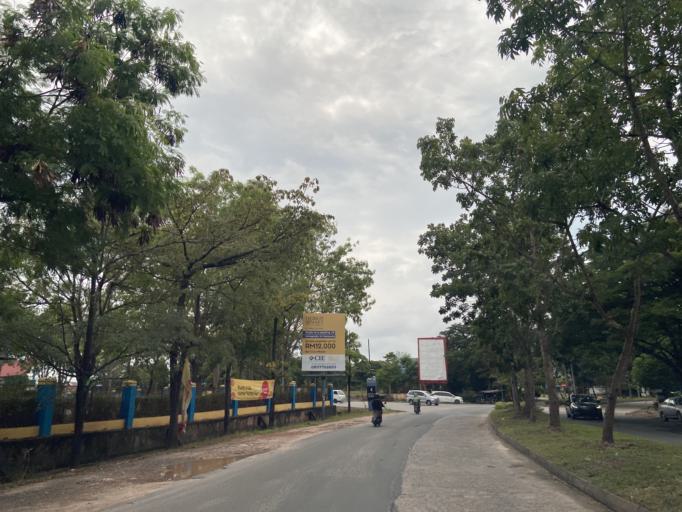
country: SG
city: Singapore
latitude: 1.1256
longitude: 104.0452
